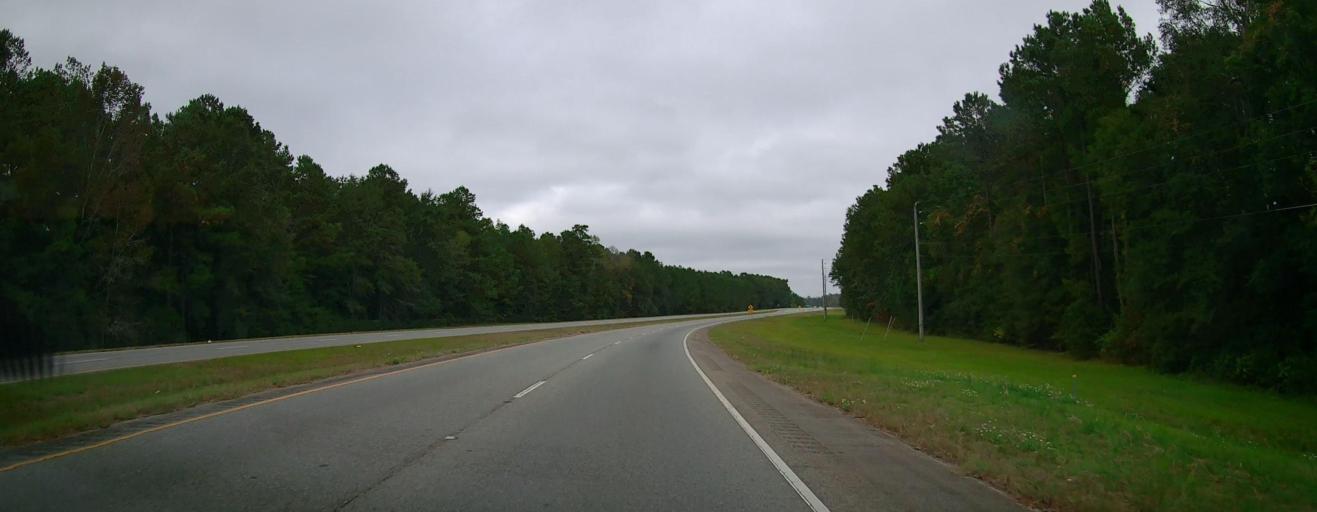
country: US
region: Georgia
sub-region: Thomas County
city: Thomasville
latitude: 30.8566
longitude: -84.0075
